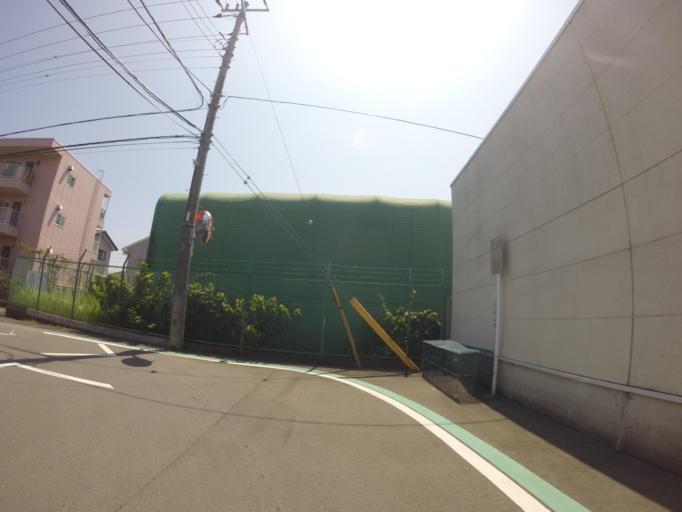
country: JP
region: Shizuoka
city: Numazu
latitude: 35.1142
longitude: 138.8739
